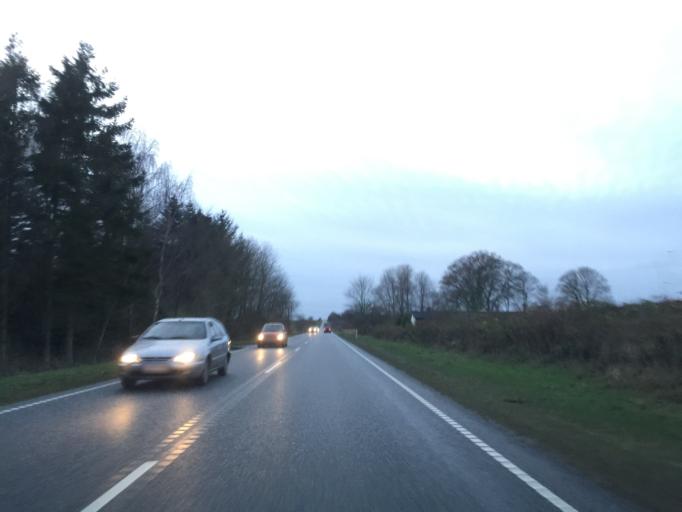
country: DK
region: Central Jutland
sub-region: Silkeborg Kommune
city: Kjellerup
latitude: 56.3122
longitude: 9.5451
